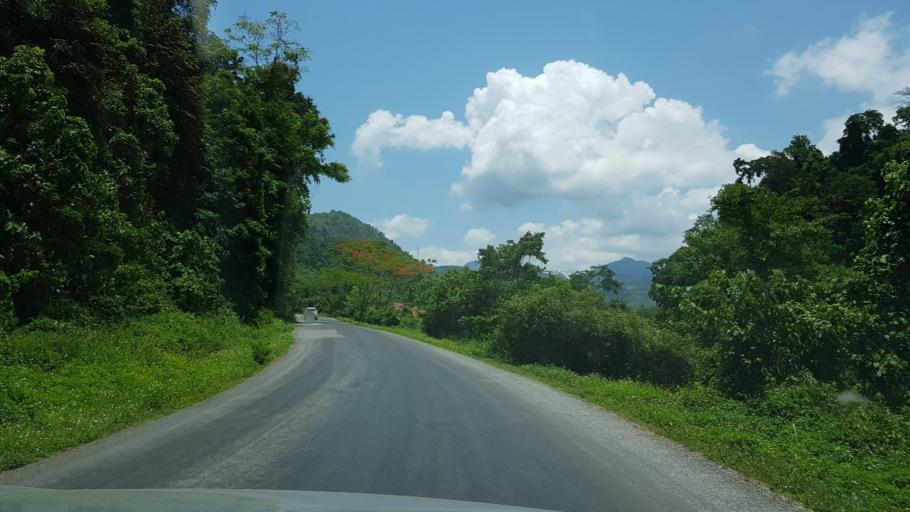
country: LA
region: Vientiane
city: Muang Kasi
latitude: 19.1240
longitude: 102.2602
